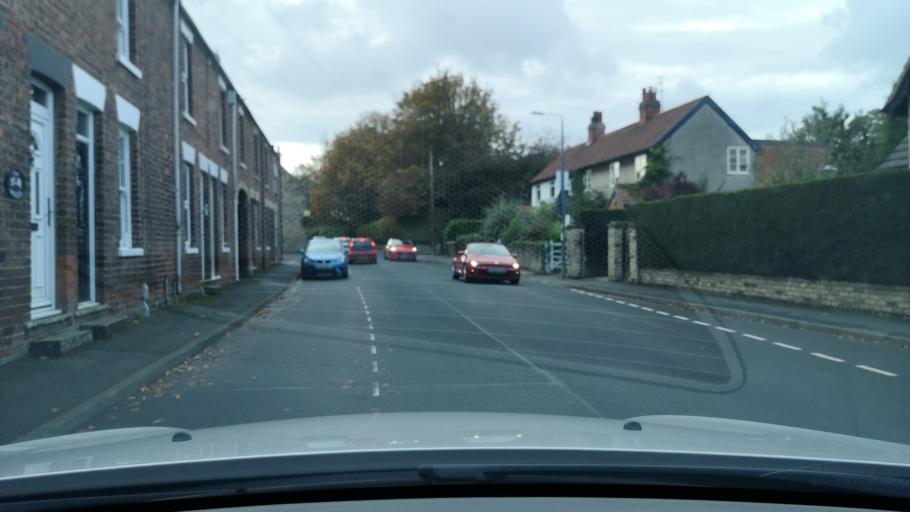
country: GB
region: England
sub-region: East Riding of Yorkshire
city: North Cave
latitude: 53.7828
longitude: -0.6410
